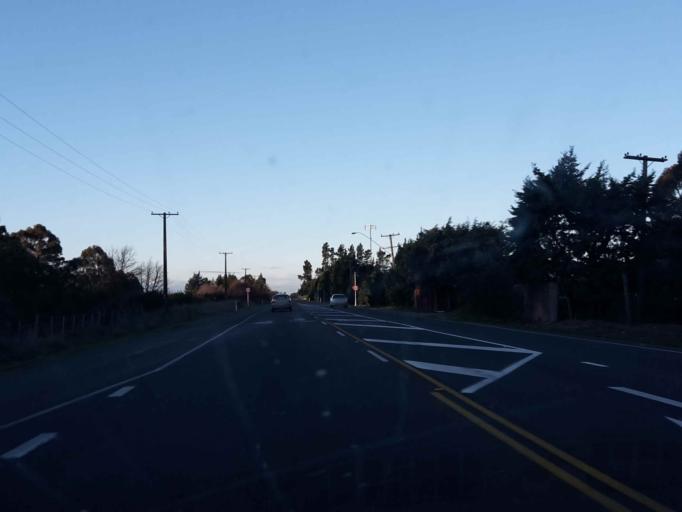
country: NZ
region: Canterbury
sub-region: Selwyn District
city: Burnham
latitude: -43.6152
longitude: 172.3148
